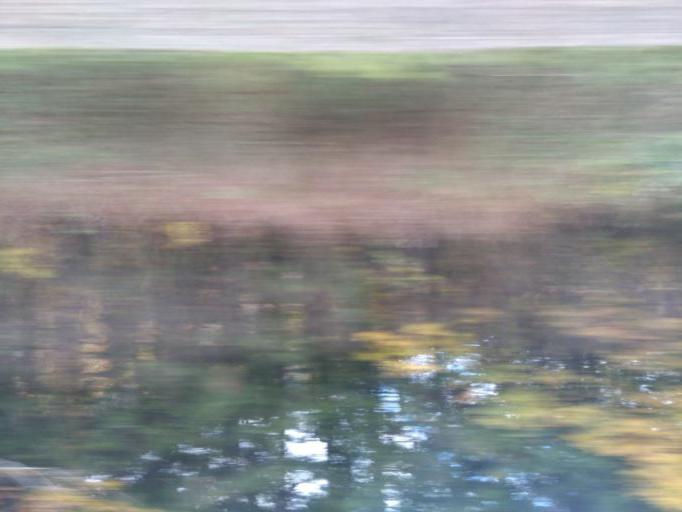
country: JP
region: Hokkaido
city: Niseko Town
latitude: 42.5962
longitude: 140.5750
